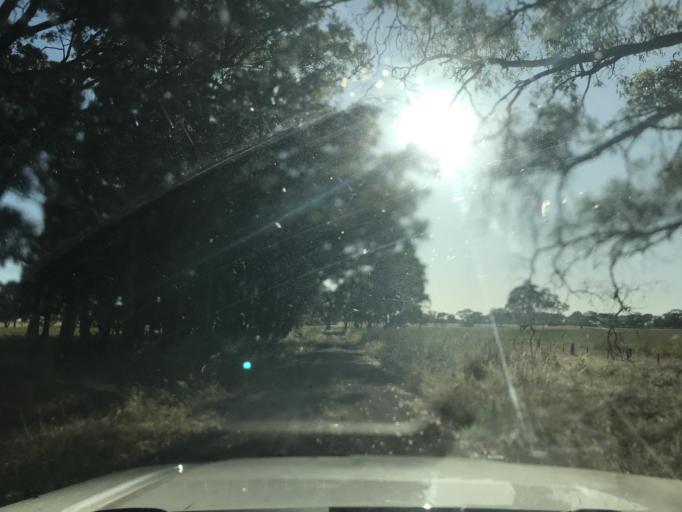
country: AU
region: South Australia
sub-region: Wattle Range
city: Penola
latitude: -37.0355
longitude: 141.3698
